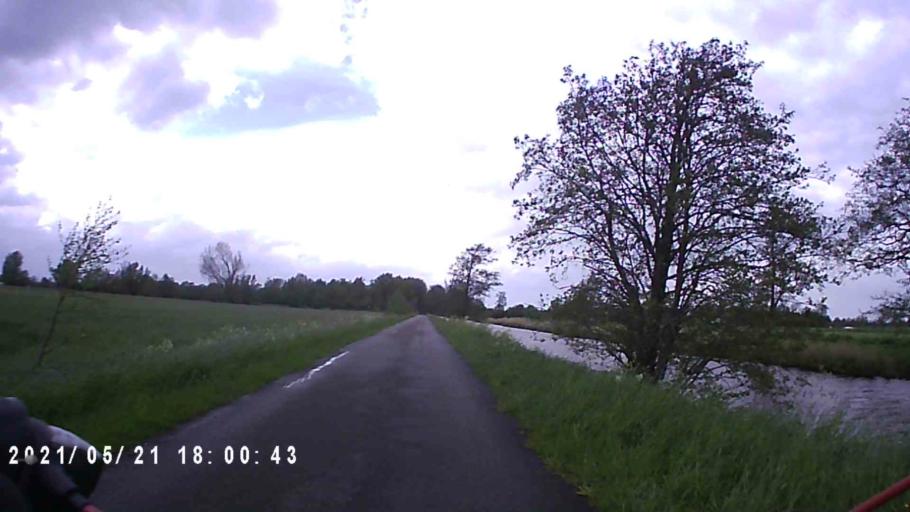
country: NL
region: Groningen
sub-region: Gemeente Leek
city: Leek
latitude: 53.1851
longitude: 6.4186
